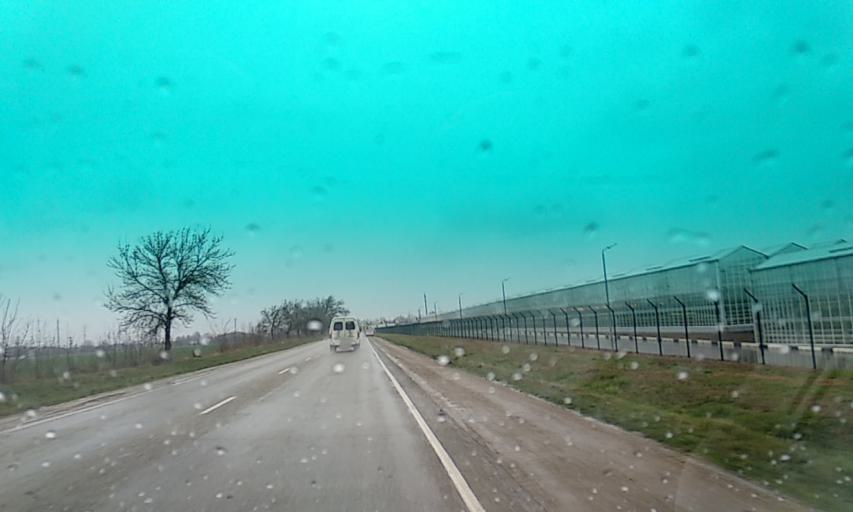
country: RU
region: Krasnodarskiy
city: Belorechensk
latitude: 44.7999
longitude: 39.8593
